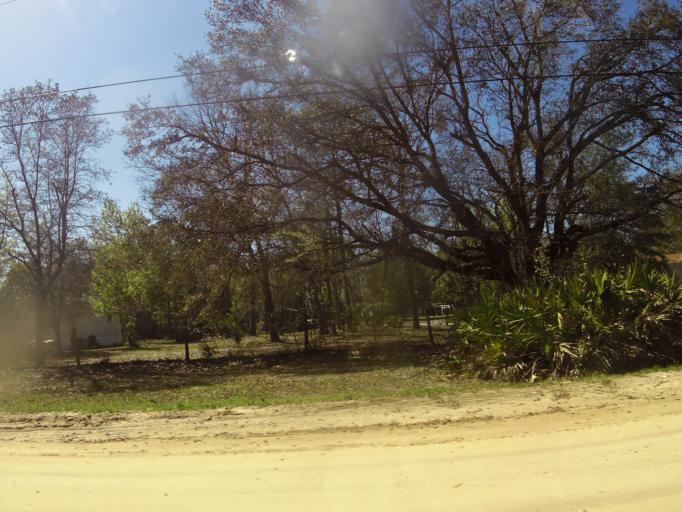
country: US
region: Florida
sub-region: Clay County
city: Middleburg
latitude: 30.1341
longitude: -81.8819
